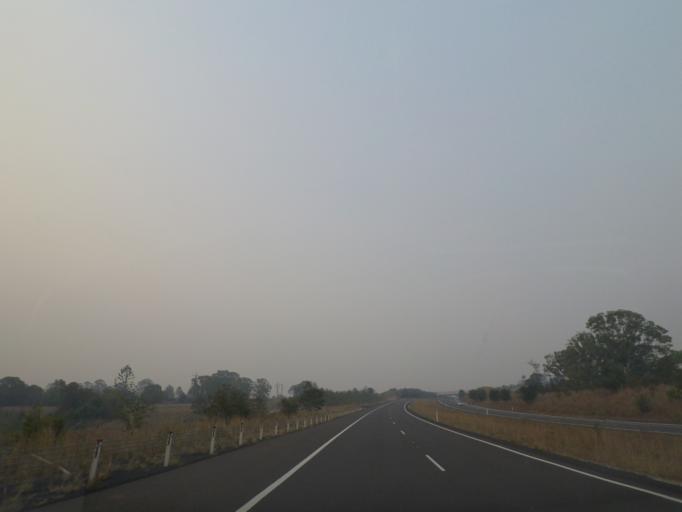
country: AU
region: New South Wales
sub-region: Nambucca Shire
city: Macksville
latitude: -30.7607
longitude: 152.9042
